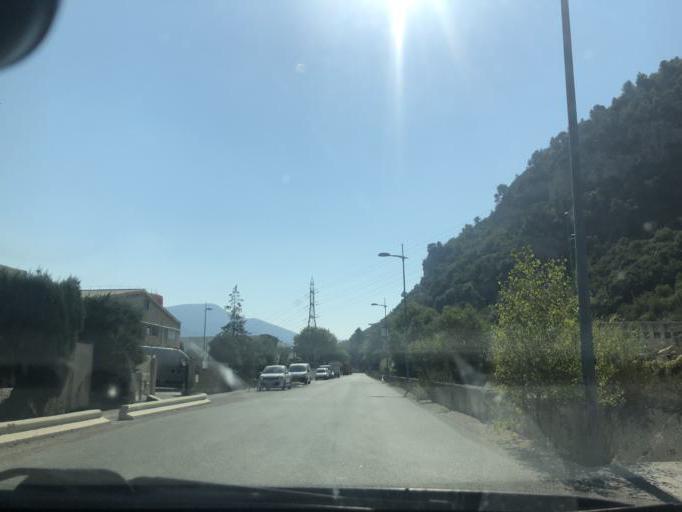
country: FR
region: Provence-Alpes-Cote d'Azur
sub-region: Departement des Alpes-Maritimes
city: Saint-Martin-du-Var
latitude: 43.8052
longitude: 7.1870
